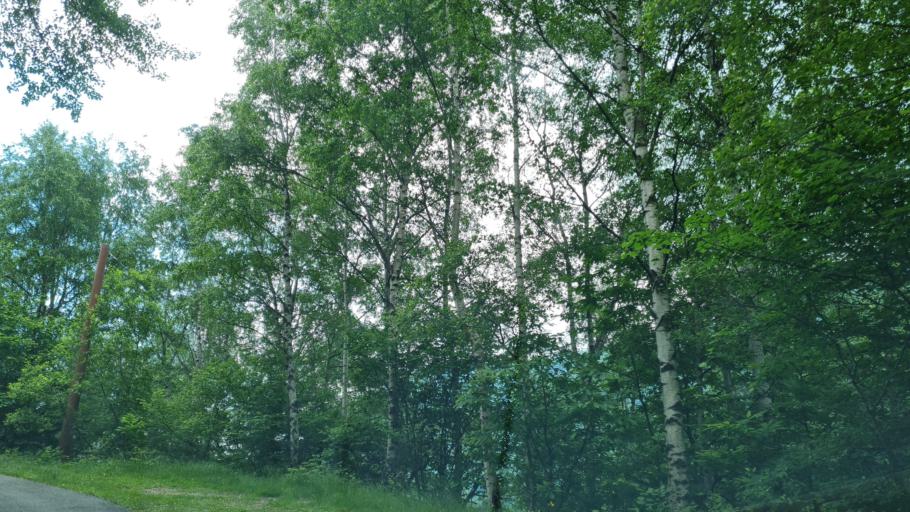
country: IT
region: Piedmont
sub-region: Provincia di Biella
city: Sordevolo
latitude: 45.5980
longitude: 7.9414
